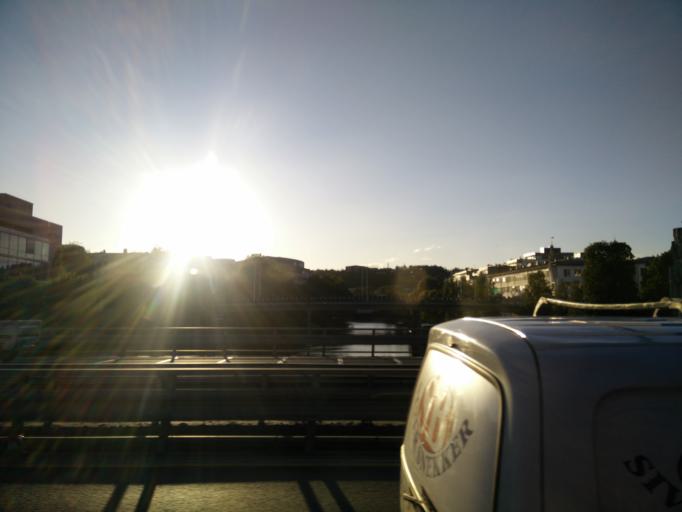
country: NO
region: Akershus
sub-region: Baerum
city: Sandvika
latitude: 59.8889
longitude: 10.5258
